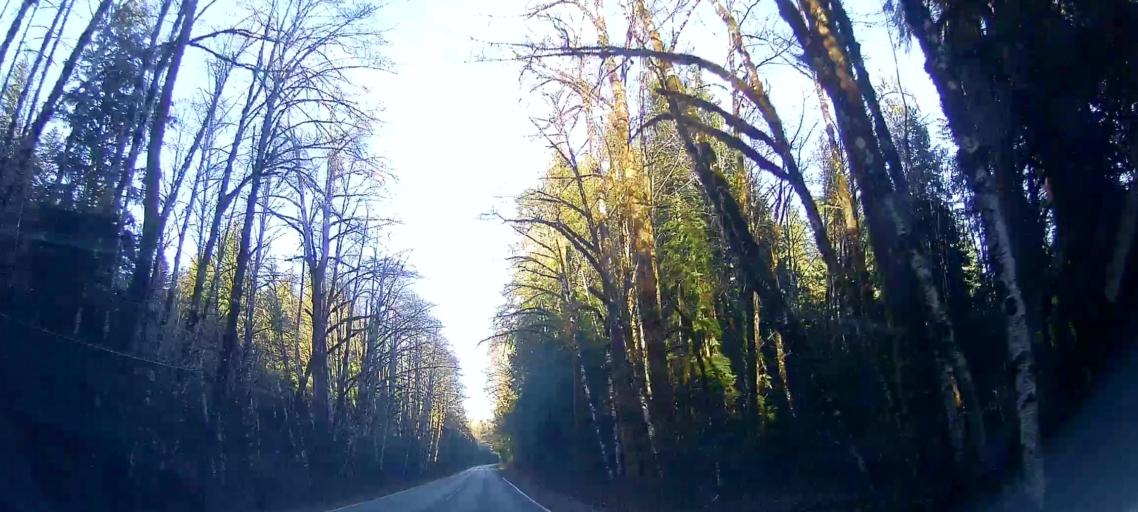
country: US
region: Washington
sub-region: Snohomish County
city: Darrington
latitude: 48.6120
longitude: -121.7543
